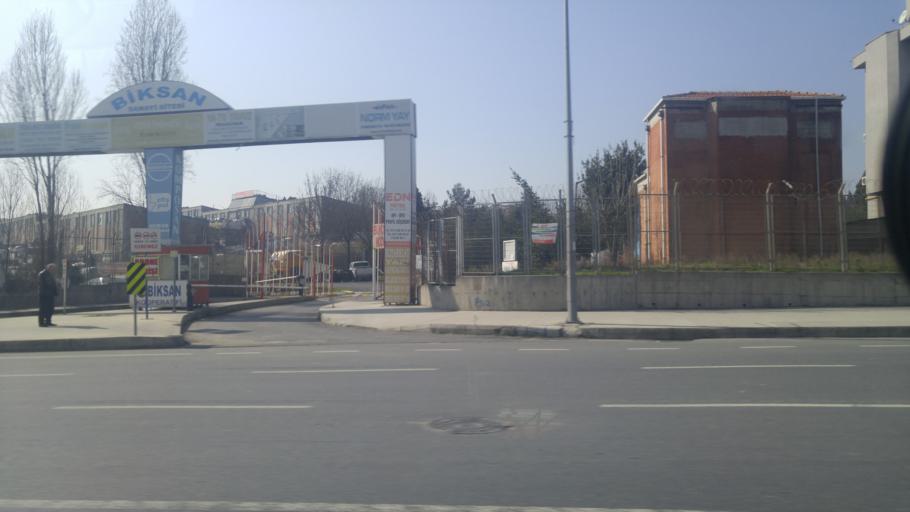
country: TR
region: Istanbul
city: Basaksehir
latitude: 41.0877
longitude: 28.7968
